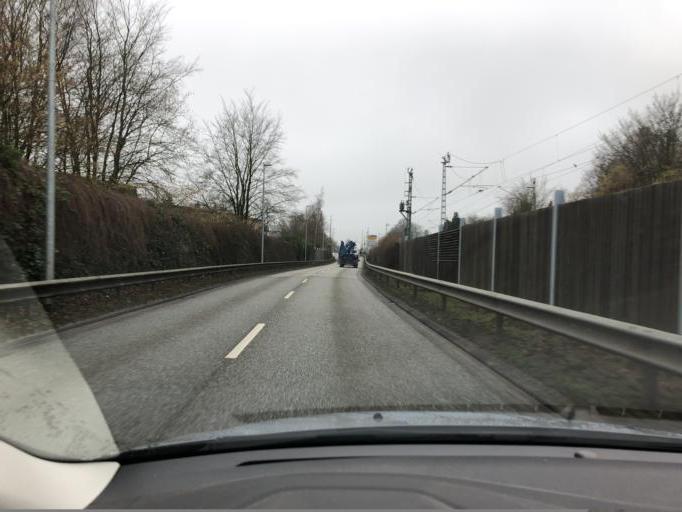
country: DE
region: Lower Saxony
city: Bad Zwischenahn
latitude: 53.1812
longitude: 8.0122
